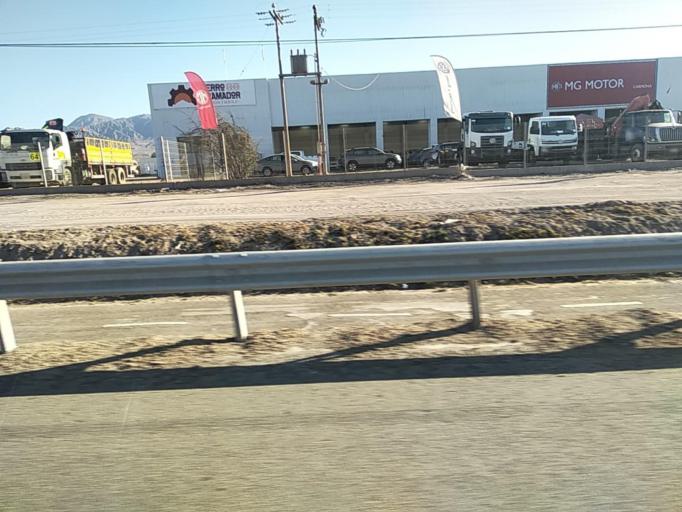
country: CL
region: Atacama
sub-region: Provincia de Copiapo
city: Copiapo
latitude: -27.3315
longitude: -70.3845
